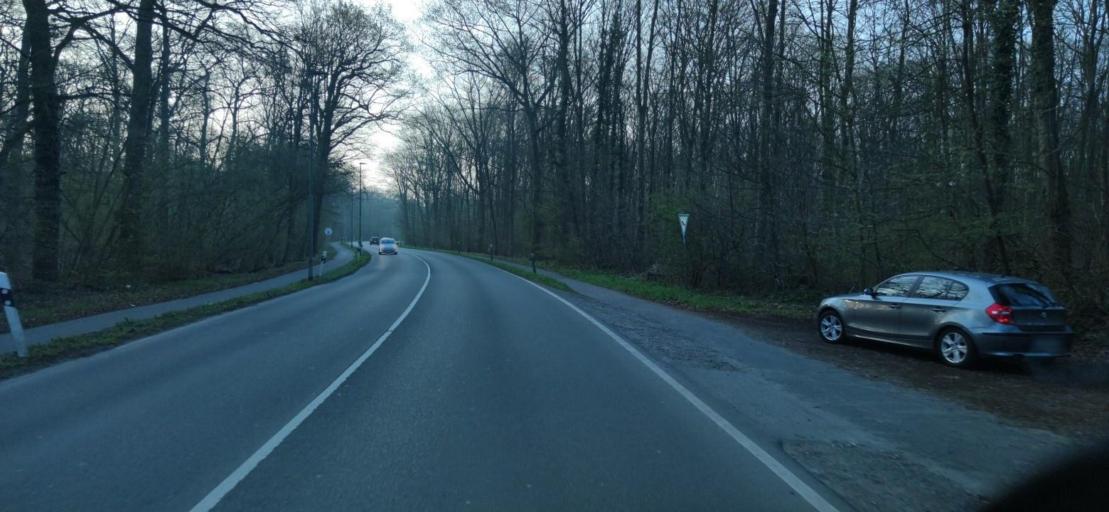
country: DE
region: North Rhine-Westphalia
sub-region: Regierungsbezirk Dusseldorf
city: Voerde
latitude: 51.5793
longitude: 6.7038
